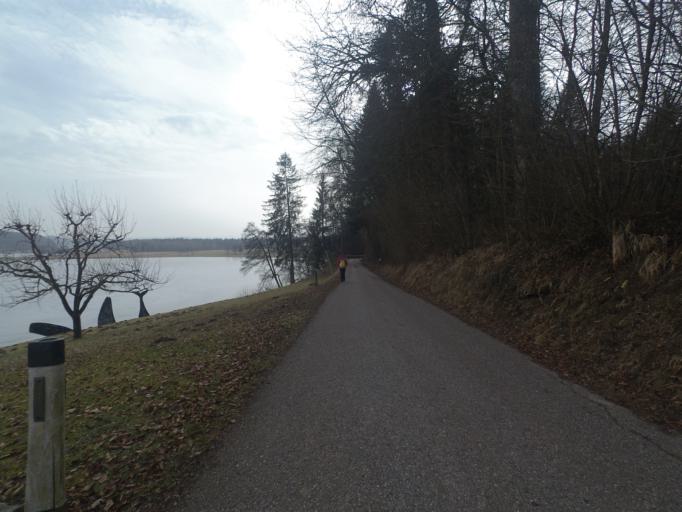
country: AT
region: Salzburg
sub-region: Politischer Bezirk Salzburg-Umgebung
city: Lamprechtshausen
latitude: 48.0721
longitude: 12.9463
